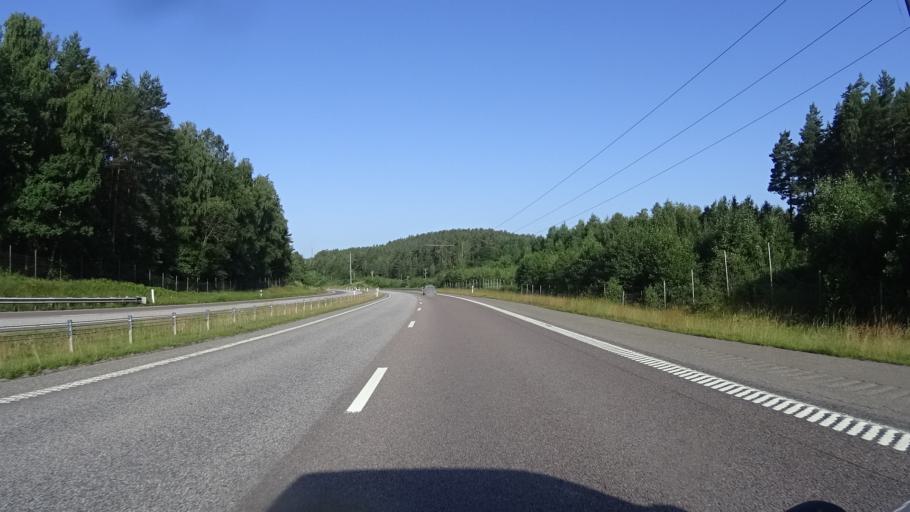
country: SE
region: OEstergoetland
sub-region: Norrkopings Kommun
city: Jursla
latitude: 58.6719
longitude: 16.2270
